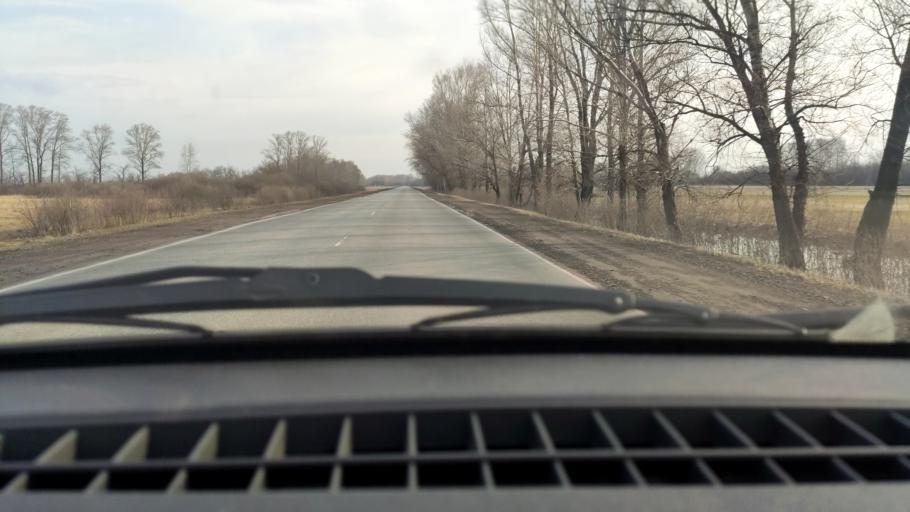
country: RU
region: Bashkortostan
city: Chishmy
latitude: 54.4019
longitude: 55.2137
